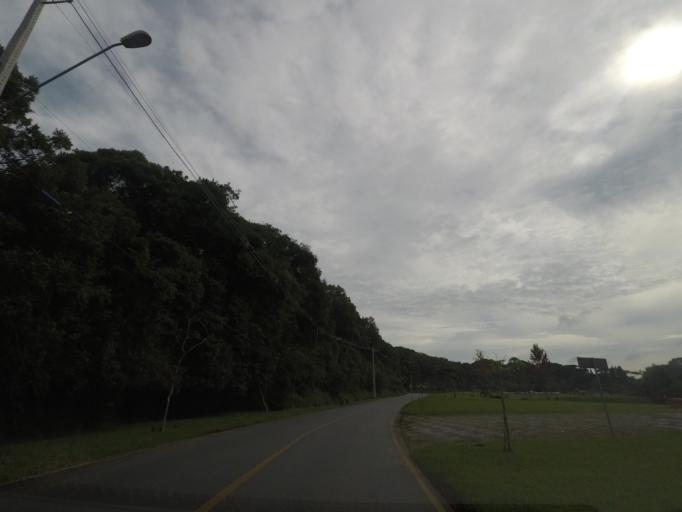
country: BR
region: Parana
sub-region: Curitiba
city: Curitiba
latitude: -25.3917
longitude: -49.3066
